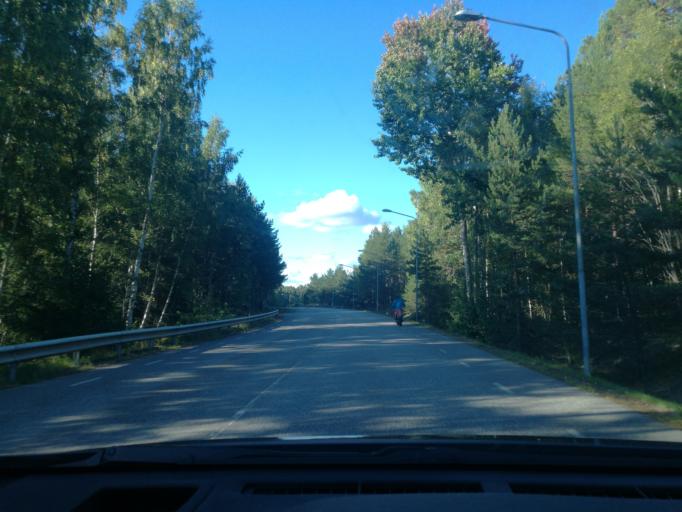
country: SE
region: Vaestmanland
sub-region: Kungsors Kommun
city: Kungsoer
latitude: 59.4102
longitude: 16.1085
